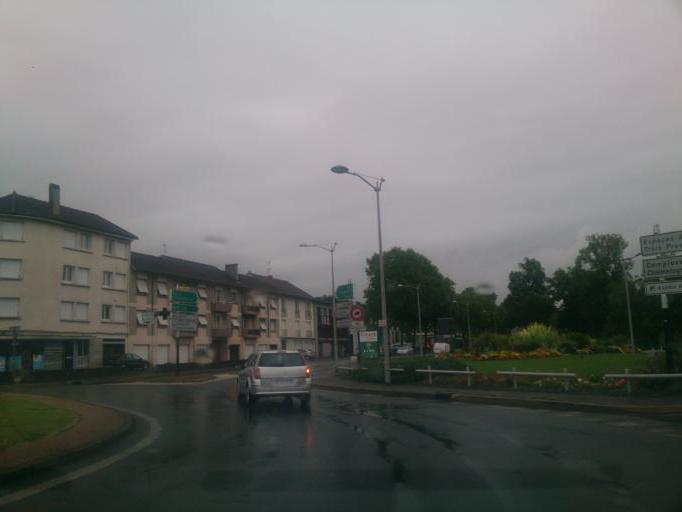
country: FR
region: Limousin
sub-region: Departement de la Correze
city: Brive-la-Gaillarde
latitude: 45.1659
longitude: 1.5418
